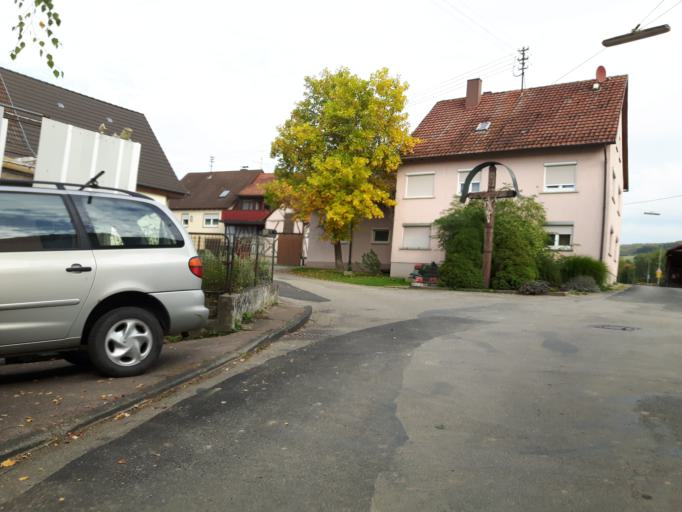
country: DE
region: Baden-Wuerttemberg
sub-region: Regierungsbezirk Stuttgart
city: Krautheim
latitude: 49.3599
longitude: 9.6026
